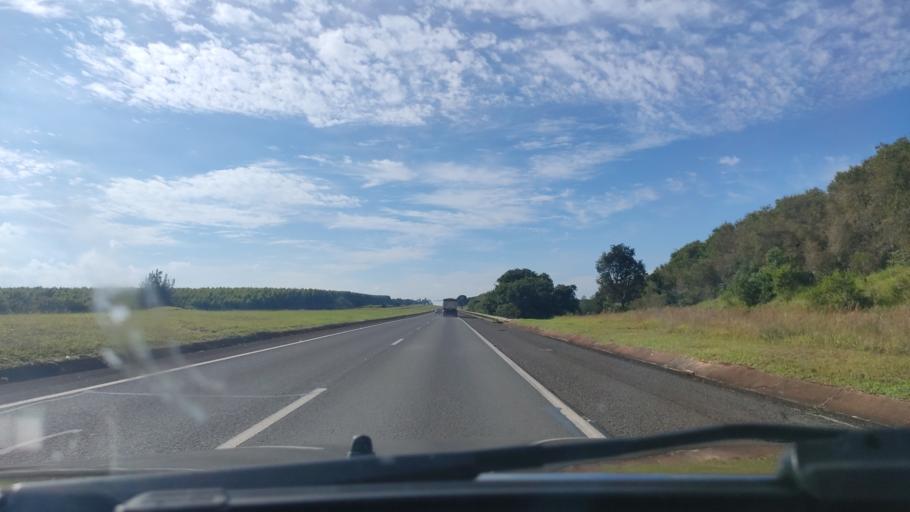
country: BR
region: Sao Paulo
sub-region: Itatinga
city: Itatinga
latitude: -23.0430
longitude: -48.6139
